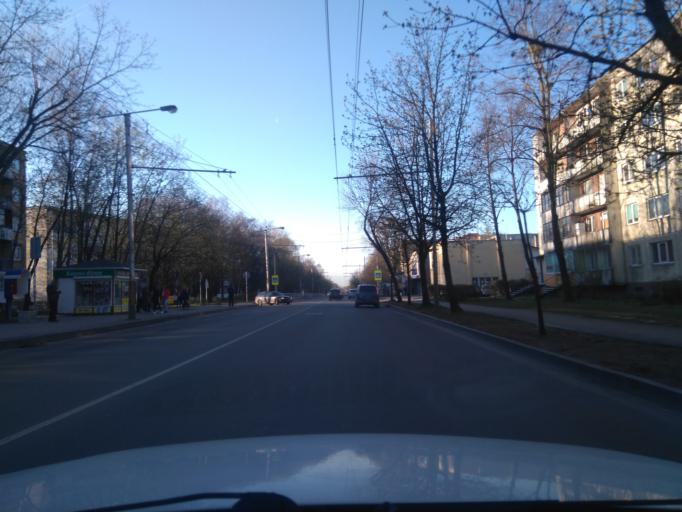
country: LT
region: Kauno apskritis
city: Dainava (Kaunas)
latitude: 54.9108
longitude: 23.9739
